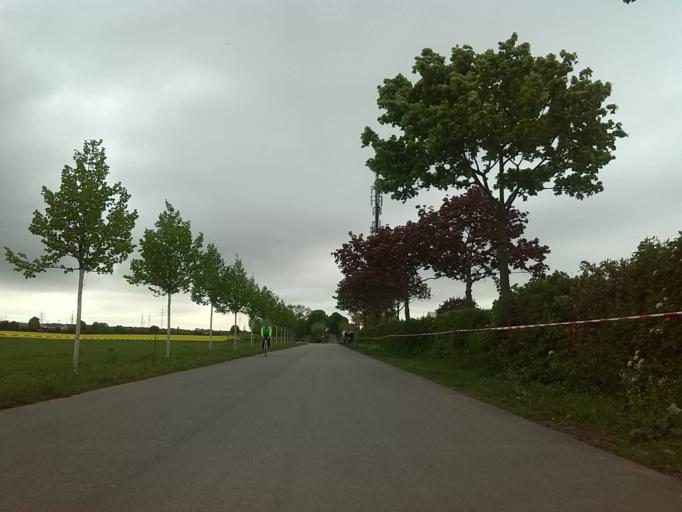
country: DE
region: Baden-Wuerttemberg
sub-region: Karlsruhe Region
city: Ilvesheim
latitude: 49.4685
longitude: 8.5298
